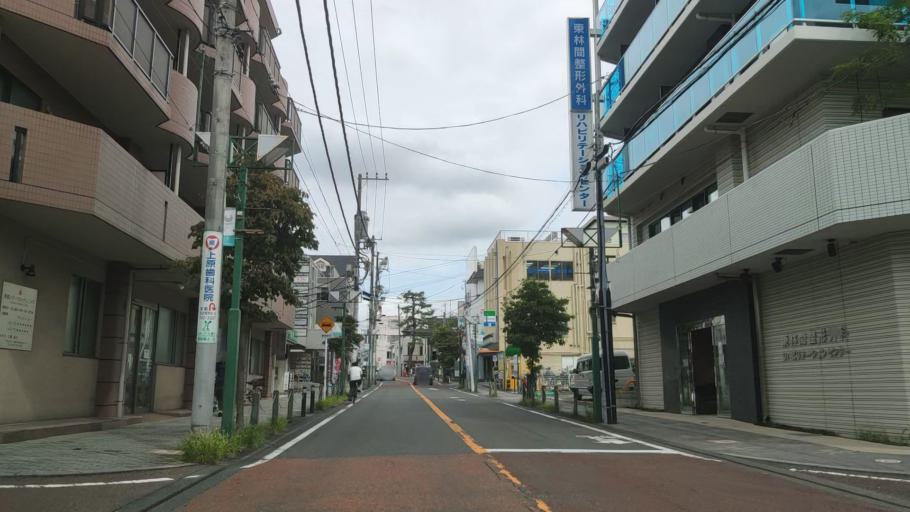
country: JP
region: Tokyo
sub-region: Machida-shi
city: Machida
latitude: 35.5205
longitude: 139.4377
